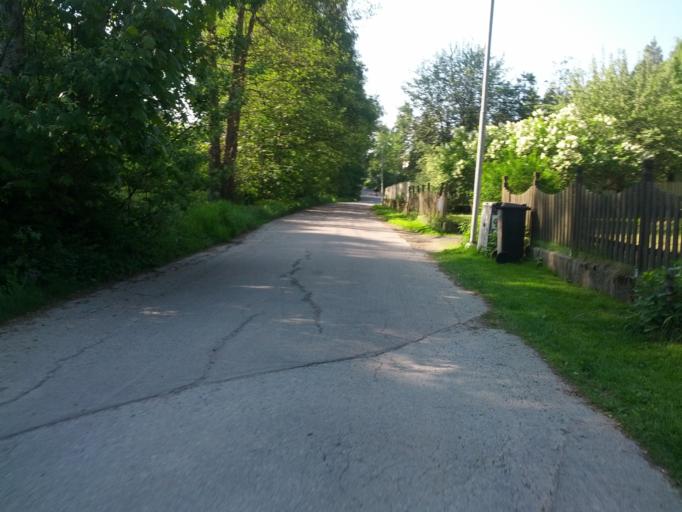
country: SE
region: Stockholm
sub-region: Taby Kommun
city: Taby
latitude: 59.4559
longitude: 18.0621
